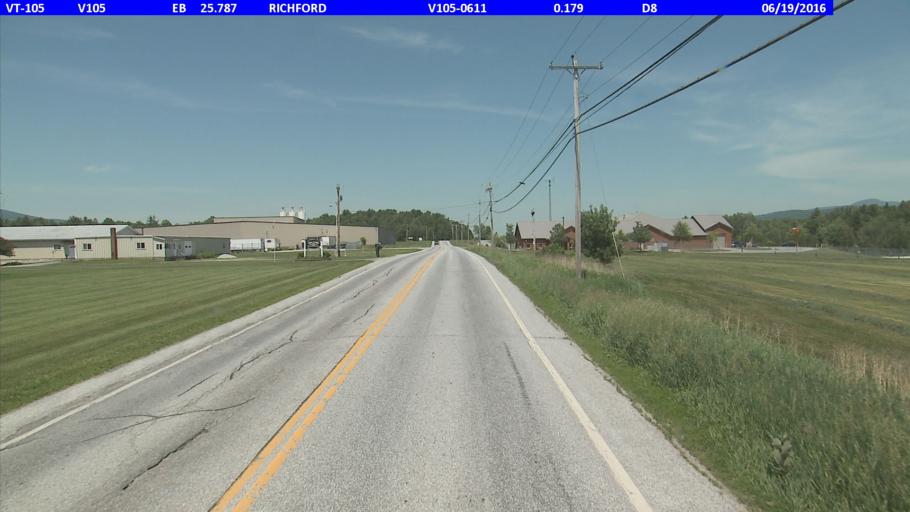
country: US
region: Vermont
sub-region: Franklin County
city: Richford
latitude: 44.9742
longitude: -72.6882
